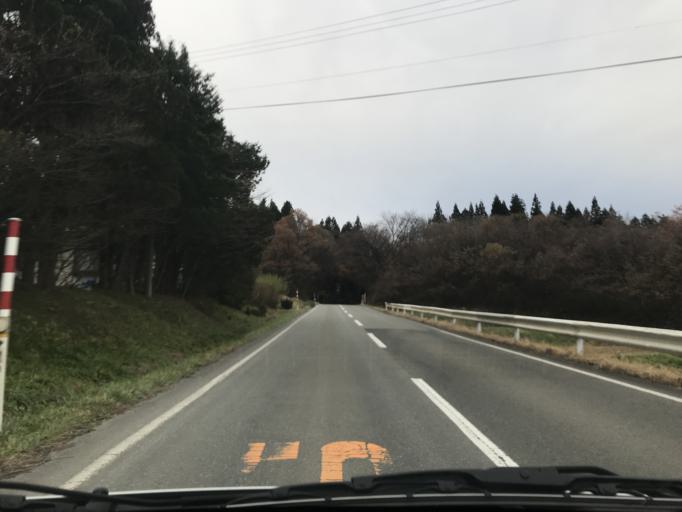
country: JP
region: Iwate
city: Kitakami
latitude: 39.2525
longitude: 141.2679
